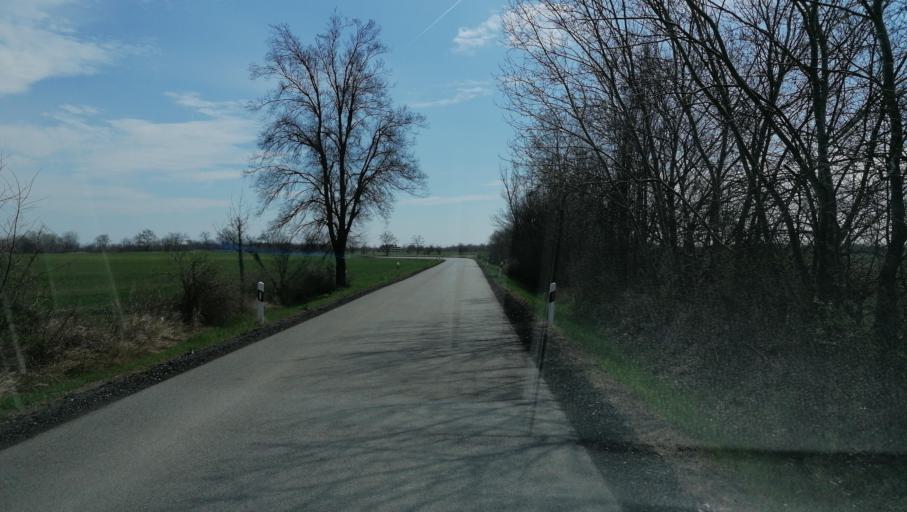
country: HU
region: Pest
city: Kiskunlachaza
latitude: 47.1925
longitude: 18.9712
